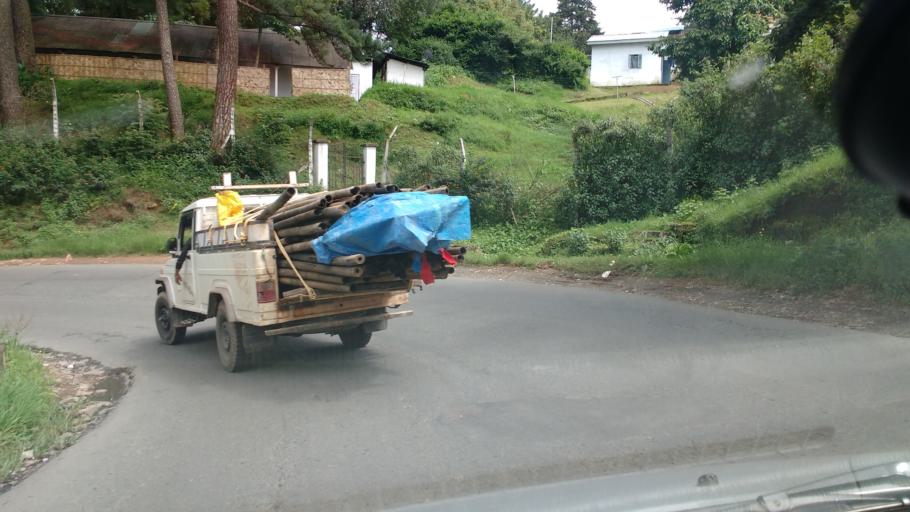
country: IN
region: Meghalaya
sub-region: East Khasi Hills
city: Shillong
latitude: 25.5715
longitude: 91.8662
